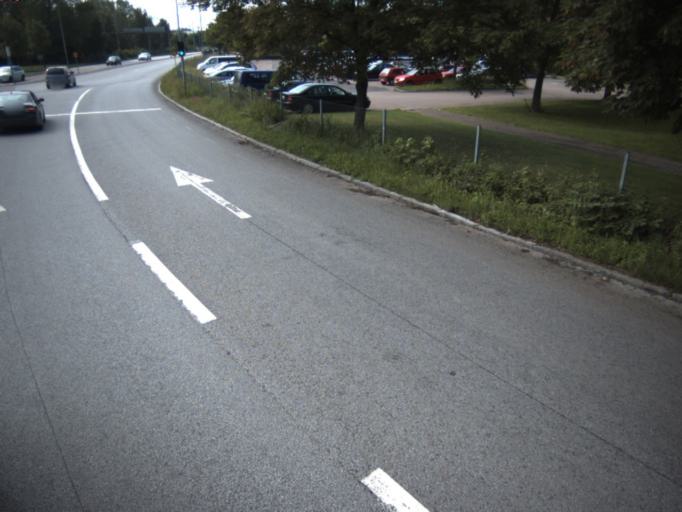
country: SE
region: Skane
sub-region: Helsingborg
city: Helsingborg
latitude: 56.0383
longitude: 12.7138
